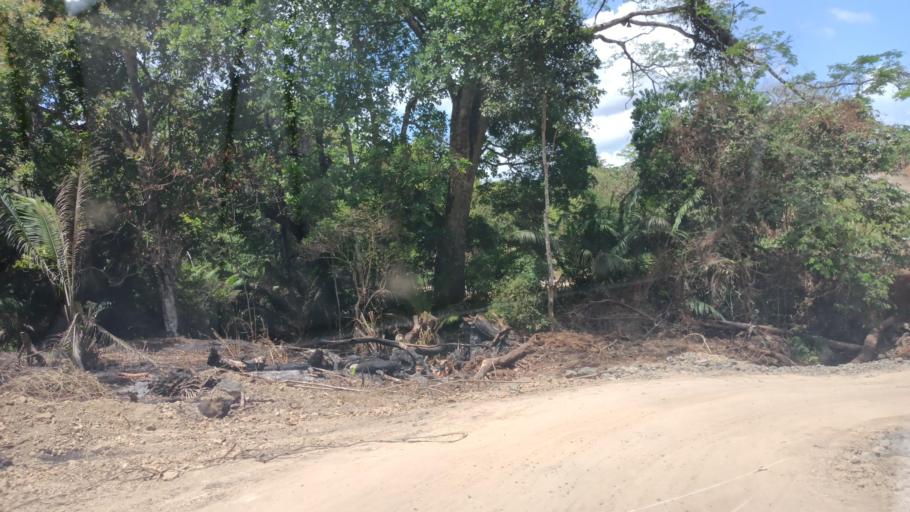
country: PA
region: Panama
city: Alcalde Diaz
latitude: 9.0800
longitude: -79.5752
